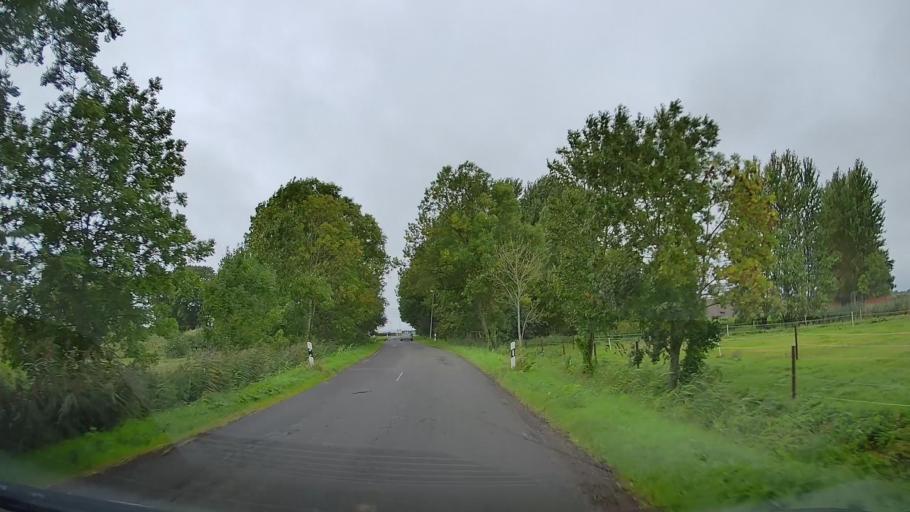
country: DE
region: Schleswig-Holstein
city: Diekhusen-Fahrstedt
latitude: 53.9185
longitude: 8.9945
